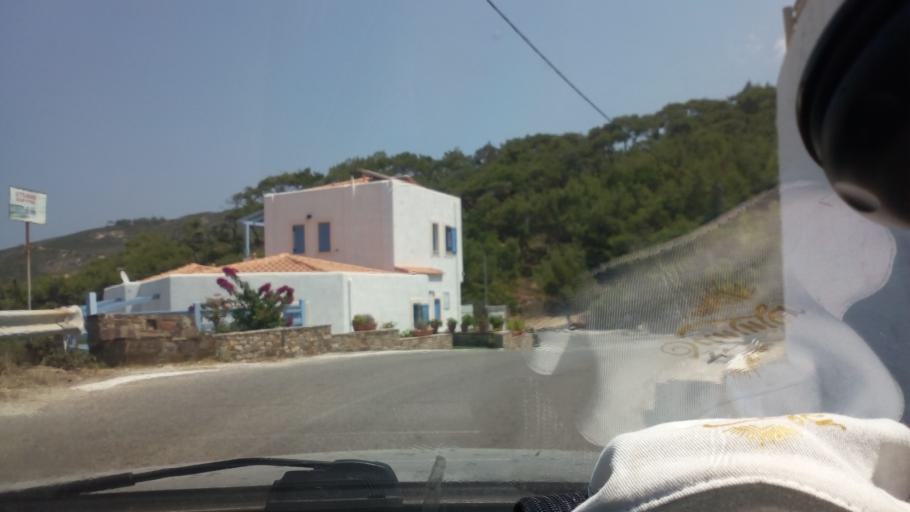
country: GR
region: North Aegean
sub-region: Nomos Samou
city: Agios Kirykos
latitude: 37.6307
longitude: 26.1033
